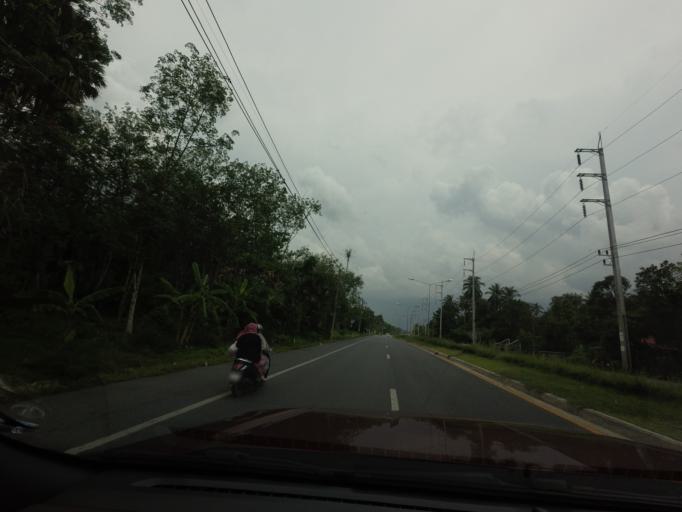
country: TH
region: Yala
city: Yala
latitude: 6.4909
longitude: 101.2651
